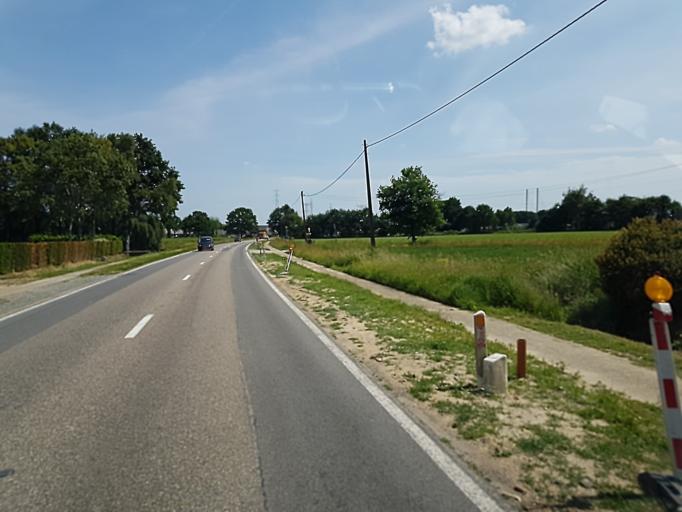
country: BE
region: Flanders
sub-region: Provincie Antwerpen
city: Westerlo
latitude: 51.1443
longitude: 4.9355
